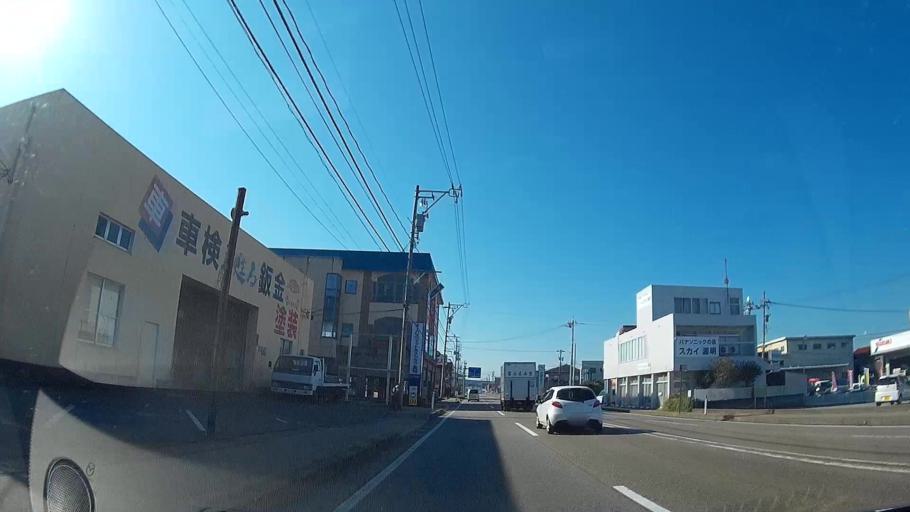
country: JP
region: Toyama
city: Takaoka
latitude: 36.7308
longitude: 137.0017
